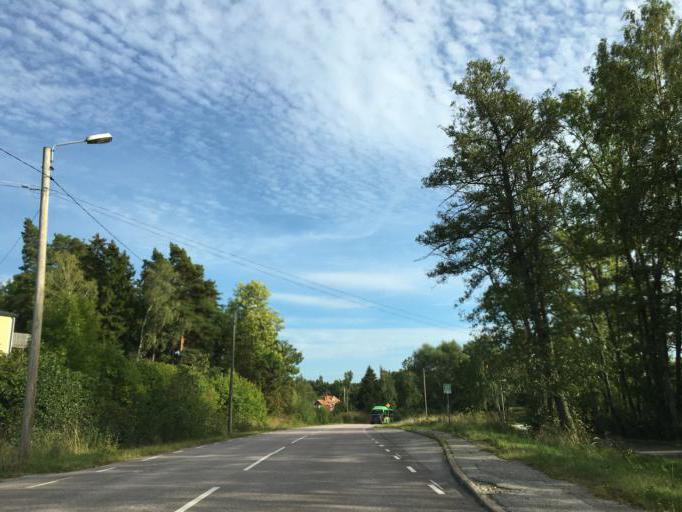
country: SE
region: Soedermanland
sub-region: Eskilstuna Kommun
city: Torshalla
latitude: 59.4393
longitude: 16.4587
